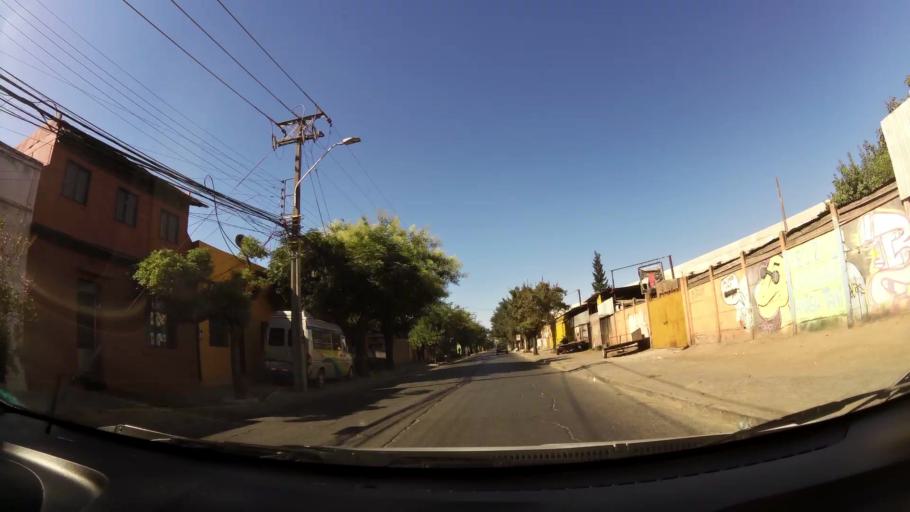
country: CL
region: O'Higgins
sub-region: Provincia de Cachapoal
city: Rancagua
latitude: -34.1649
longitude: -70.7466
